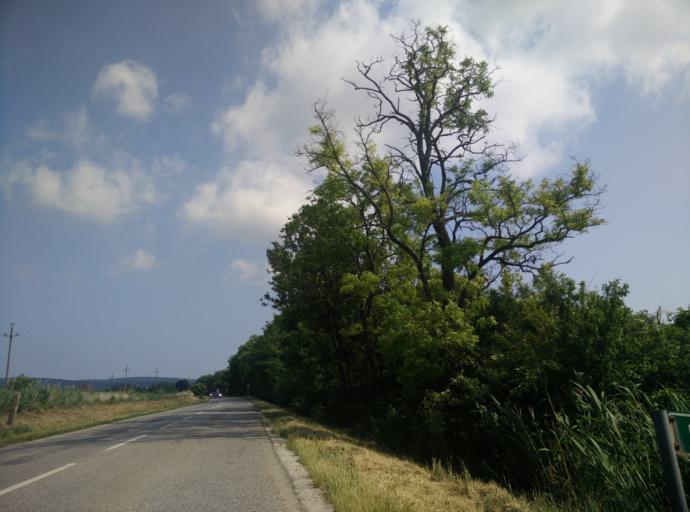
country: HU
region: Pest
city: Biatorbagy
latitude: 47.4765
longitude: 18.7925
